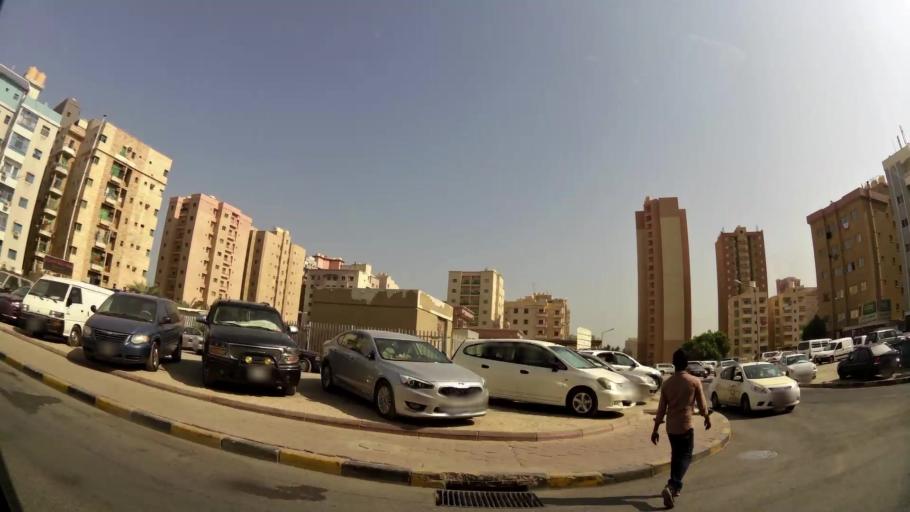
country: KW
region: Muhafazat Hawalli
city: Hawalli
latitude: 29.3364
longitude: 48.0304
